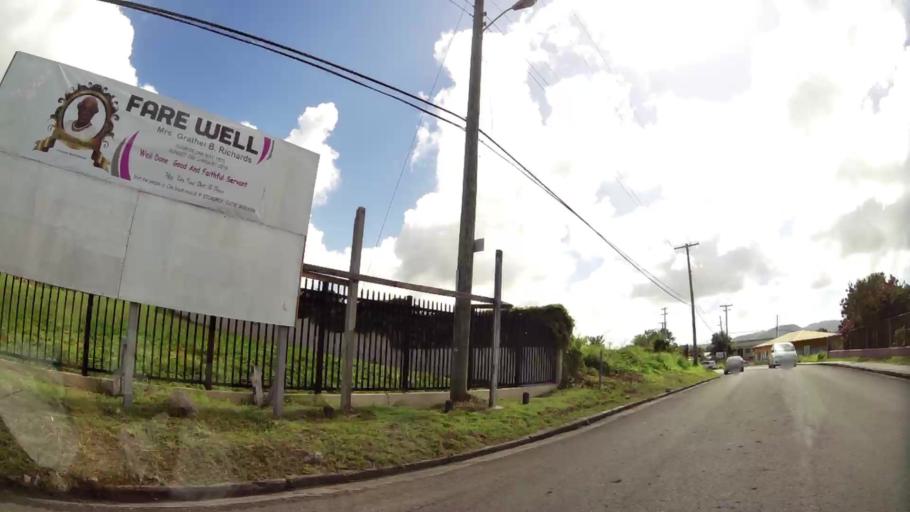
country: AG
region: Saint John
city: Saint John's
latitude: 17.1162
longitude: -61.8404
